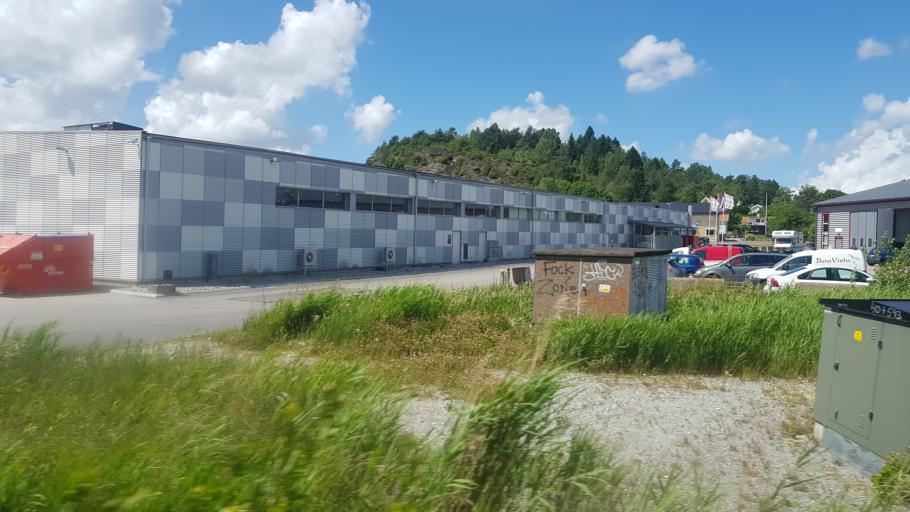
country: SE
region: Vaestra Goetaland
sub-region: Stenungsunds Kommun
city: Stora Hoga
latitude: 58.0153
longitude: 11.8339
